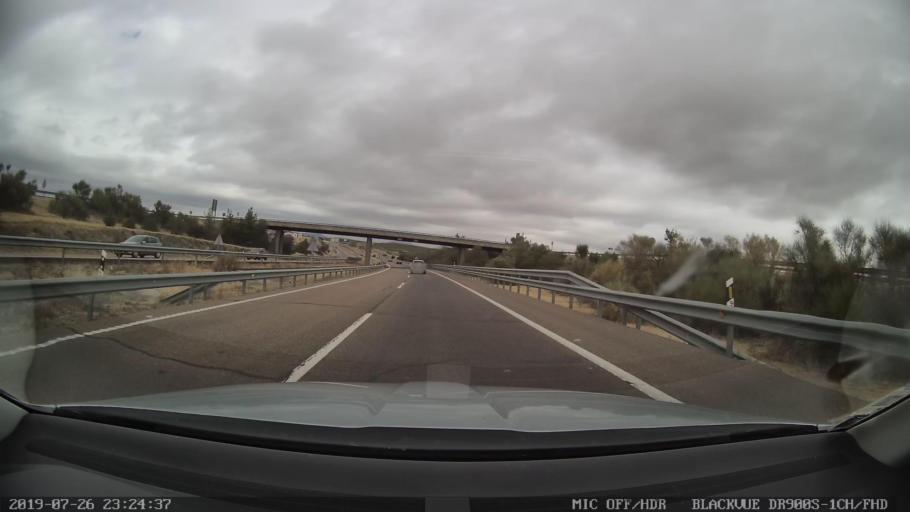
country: ES
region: Extremadura
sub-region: Provincia de Caceres
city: Escurial
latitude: 39.1745
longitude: -5.8978
